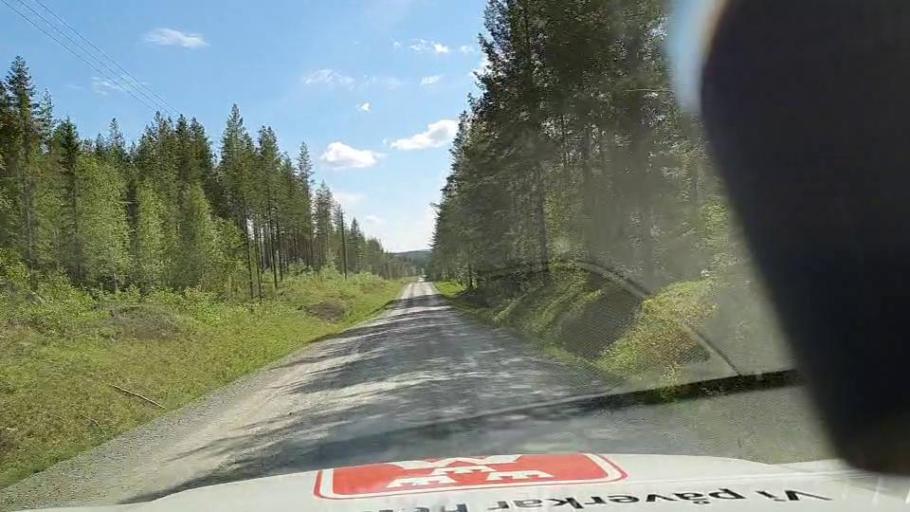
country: SE
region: Jaemtland
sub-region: Stroemsunds Kommun
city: Stroemsund
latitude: 64.4744
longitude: 15.5935
